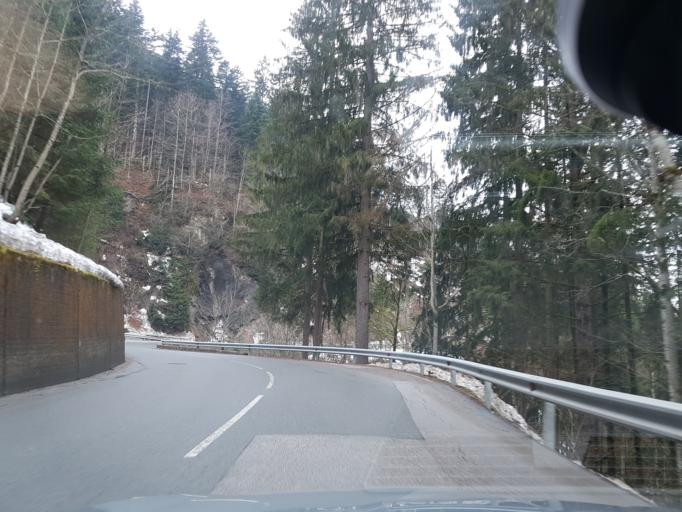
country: AT
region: Tyrol
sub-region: Politischer Bezirk Kufstein
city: Worgl
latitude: 47.4693
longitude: 12.0814
